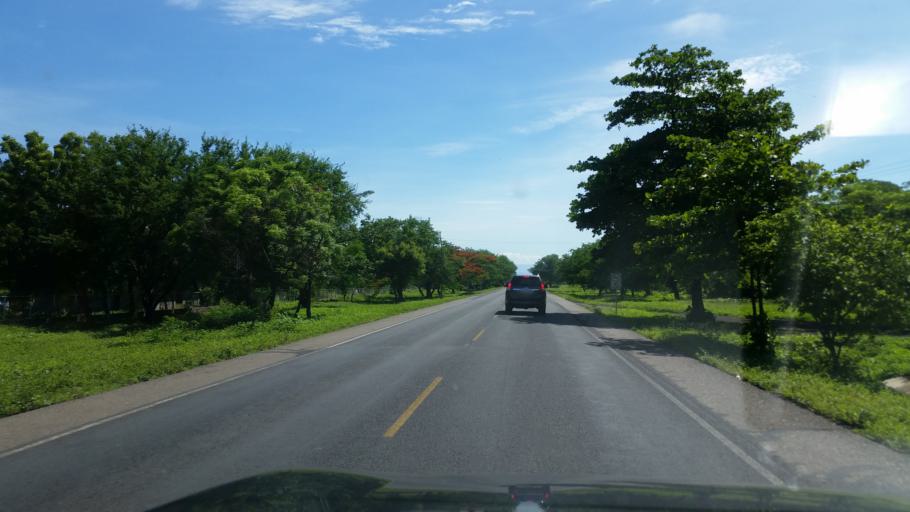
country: NI
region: Chinandega
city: El Viejo
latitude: 12.7552
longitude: -87.0652
